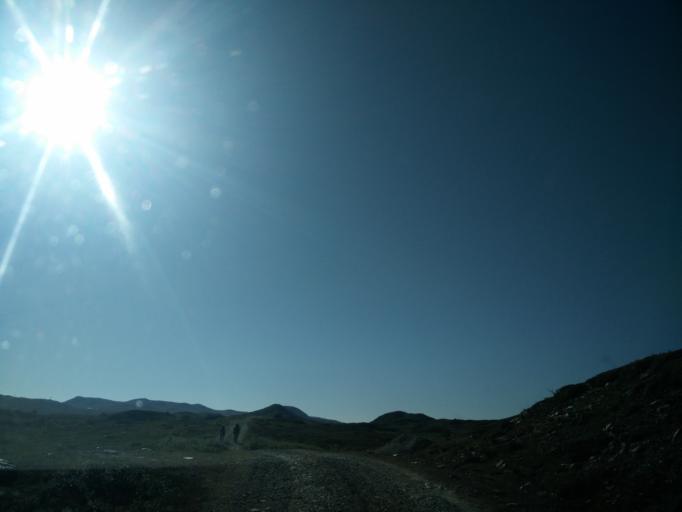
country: NO
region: Sor-Trondelag
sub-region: Tydal
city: Aas
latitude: 62.5691
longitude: 12.1970
